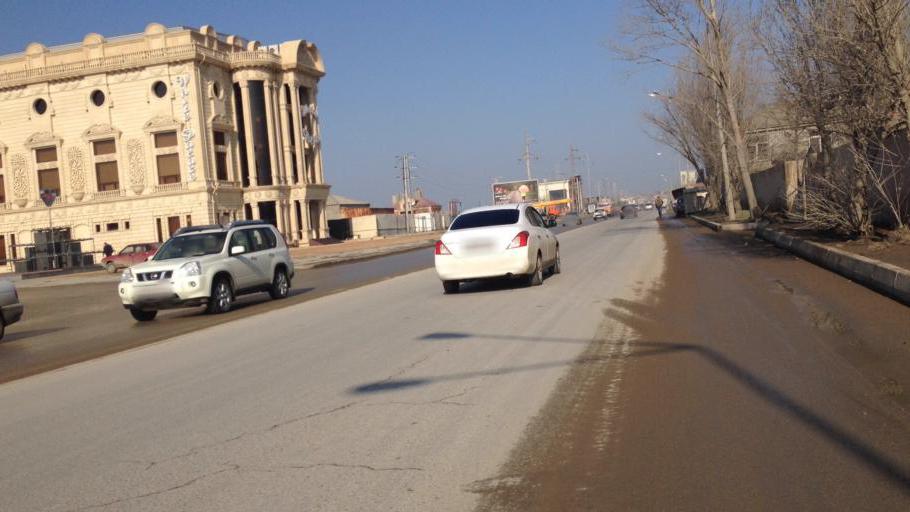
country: AZ
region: Baki
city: Binagadi
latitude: 40.4453
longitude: 49.8443
